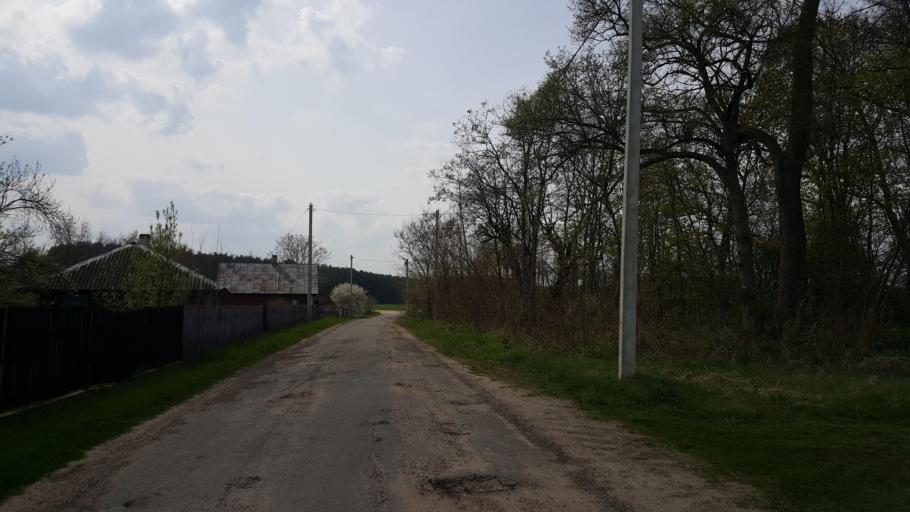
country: BY
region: Brest
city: Zhabinka
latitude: 52.2197
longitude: 23.9198
